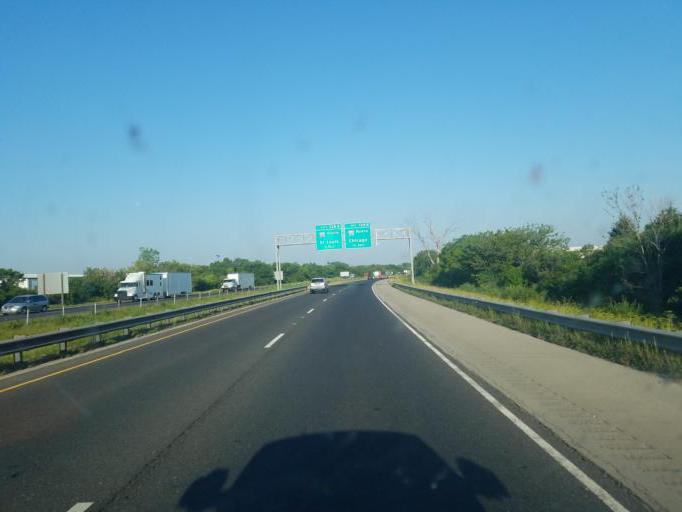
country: US
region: Illinois
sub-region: Will County
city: Shorewood
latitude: 41.4873
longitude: -88.1781
